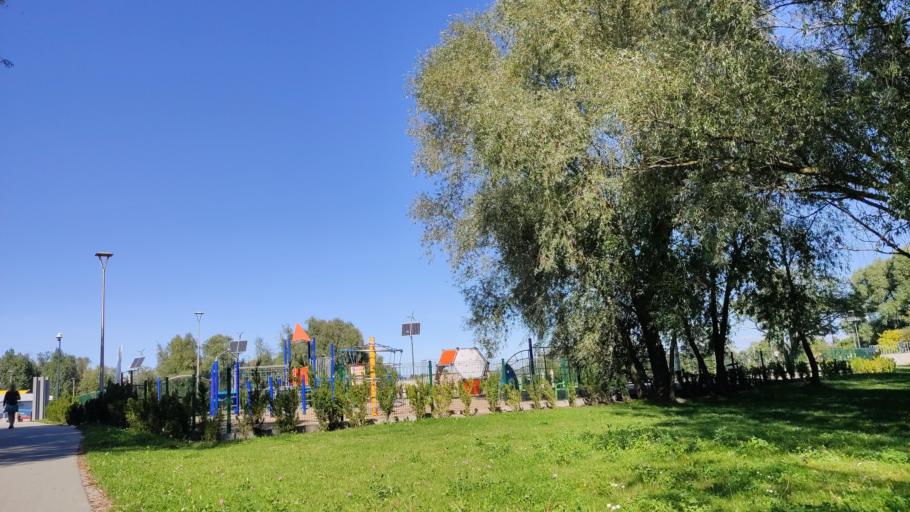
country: PL
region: Kujawsko-Pomorskie
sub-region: Powiat zninski
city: Barcin
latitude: 52.8582
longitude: 17.9446
